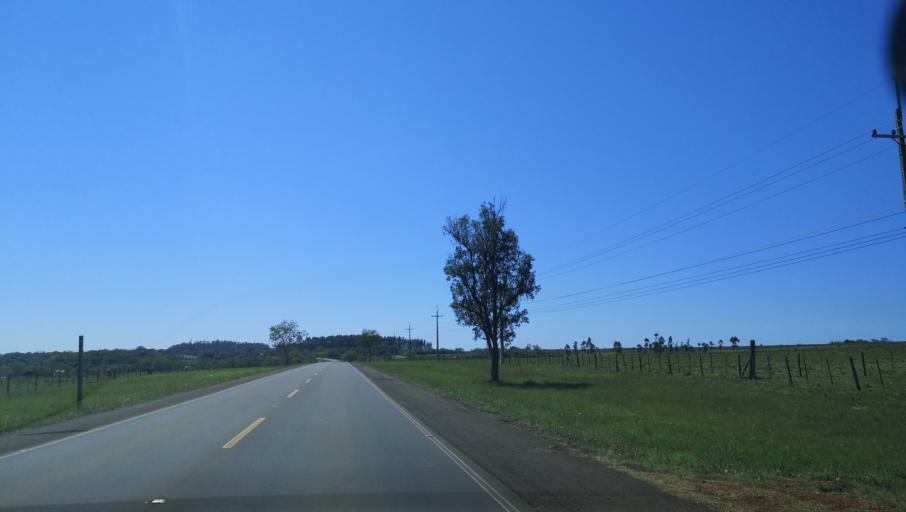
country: PY
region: Itapua
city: Carmen del Parana
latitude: -27.2209
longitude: -56.1086
